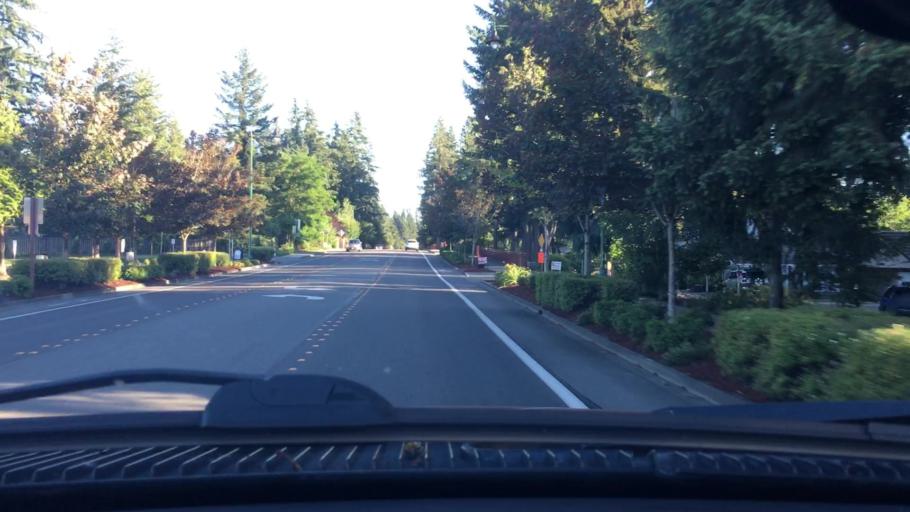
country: US
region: Washington
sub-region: King County
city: Maple Valley
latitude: 47.3841
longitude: -122.0482
